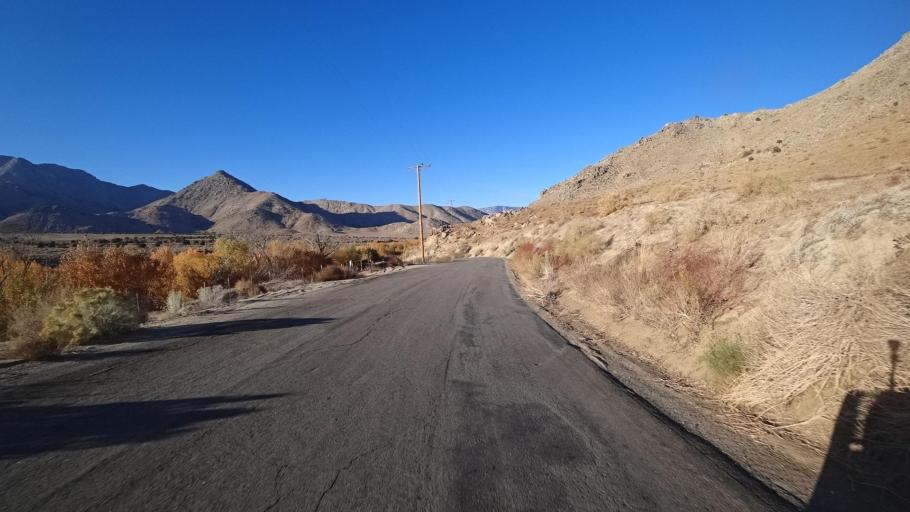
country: US
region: California
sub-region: Kern County
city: Weldon
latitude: 35.5726
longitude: -118.2505
